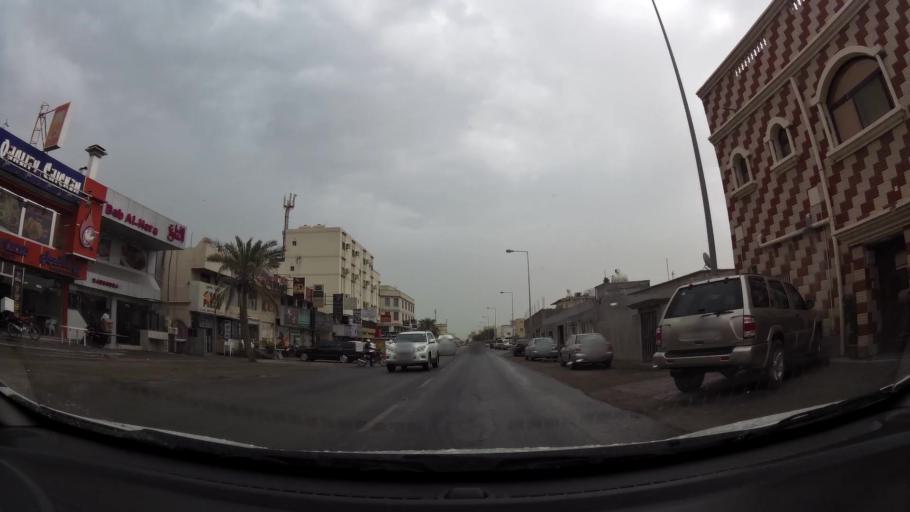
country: BH
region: Northern
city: Madinat `Isa
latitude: 26.1657
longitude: 50.5696
